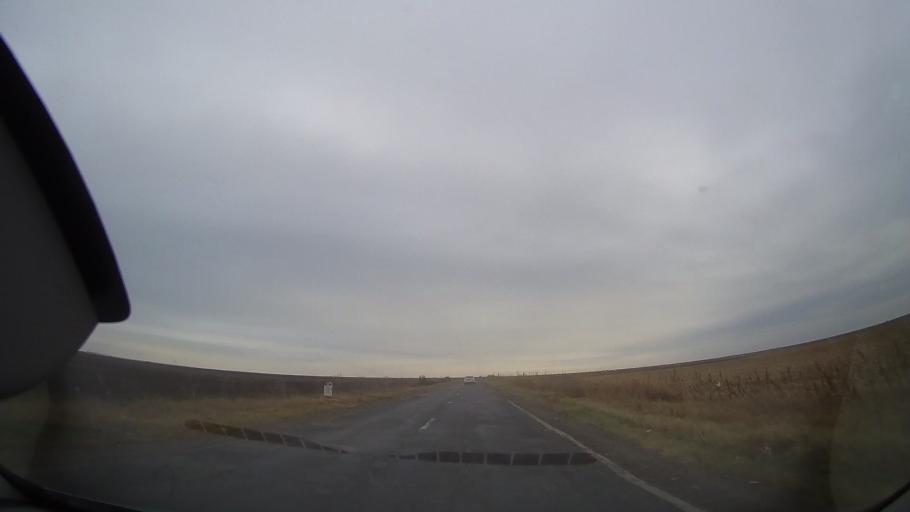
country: RO
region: Ialomita
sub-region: Oras Amara
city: Amara
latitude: 44.6706
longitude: 27.3009
